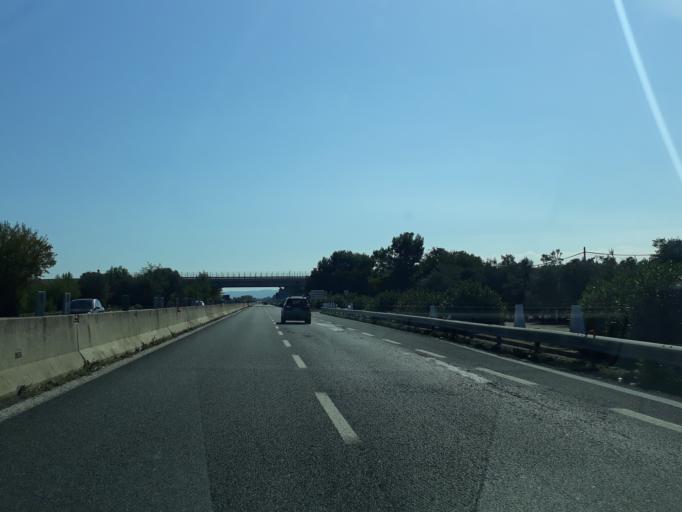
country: IT
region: Apulia
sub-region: Provincia di Bari
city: Monopoli
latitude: 40.9084
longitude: 17.3235
